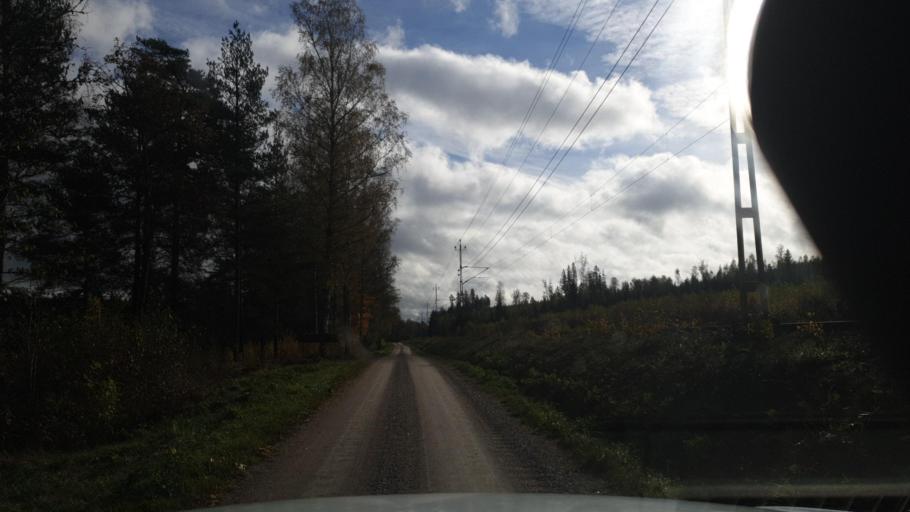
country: SE
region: Vaermland
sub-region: Sunne Kommun
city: Sunne
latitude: 59.6171
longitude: 12.9662
